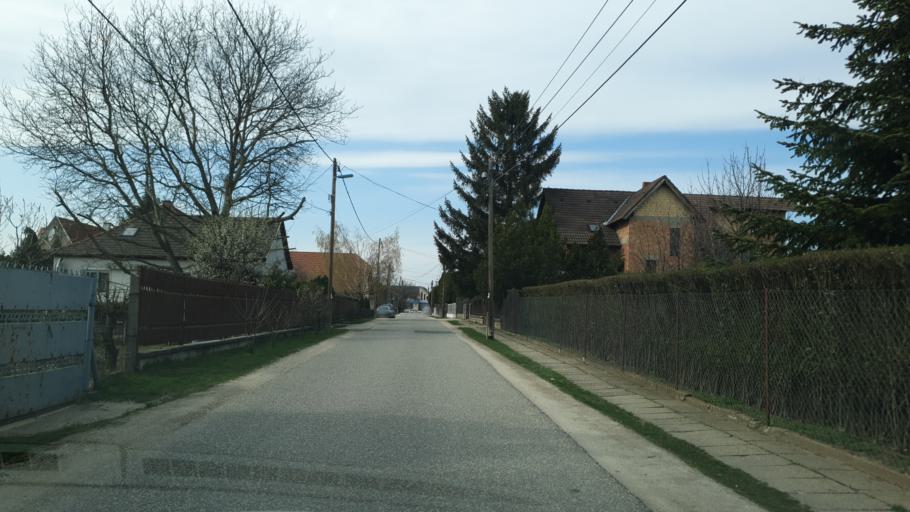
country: HU
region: Pest
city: Biatorbagy
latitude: 47.4694
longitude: 18.8265
